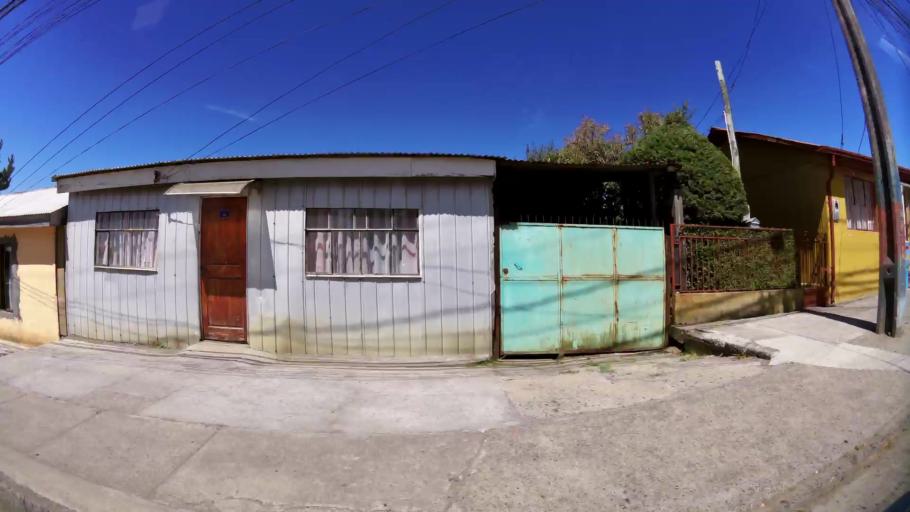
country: CL
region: Biobio
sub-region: Provincia de Concepcion
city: Penco
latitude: -36.7484
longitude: -72.9942
